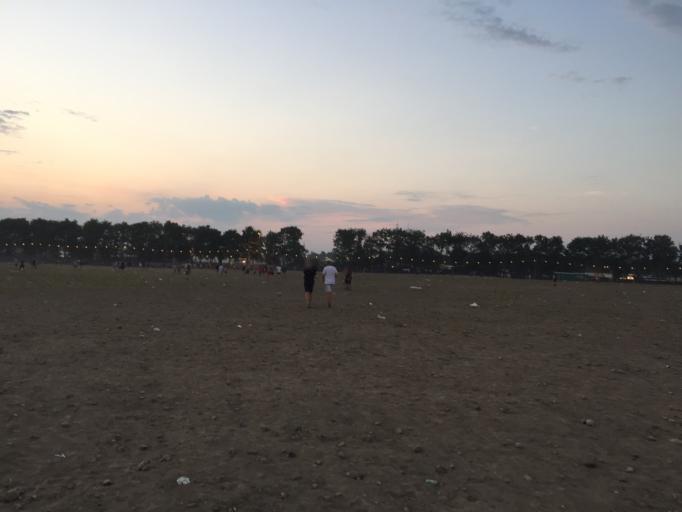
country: DK
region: Zealand
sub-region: Roskilde Kommune
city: Roskilde
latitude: 55.6174
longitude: 12.0799
